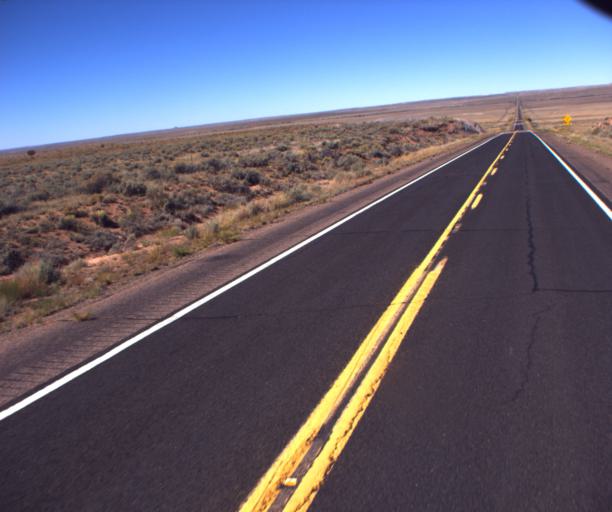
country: US
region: Arizona
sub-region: Navajo County
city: Snowflake
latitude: 34.7156
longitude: -109.7677
